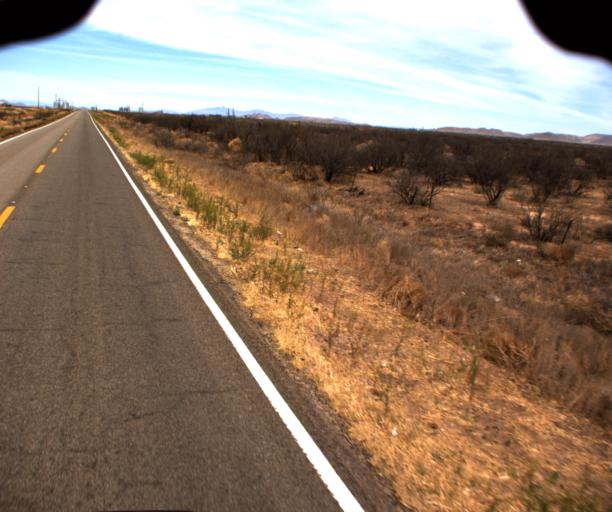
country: US
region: Arizona
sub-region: Cochise County
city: Bisbee
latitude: 31.7384
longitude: -109.6878
